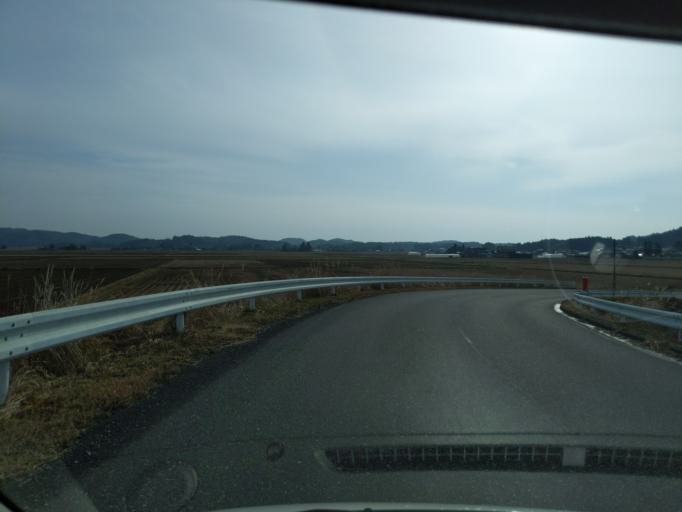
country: JP
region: Iwate
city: Ichinoseki
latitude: 38.7811
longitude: 141.1769
